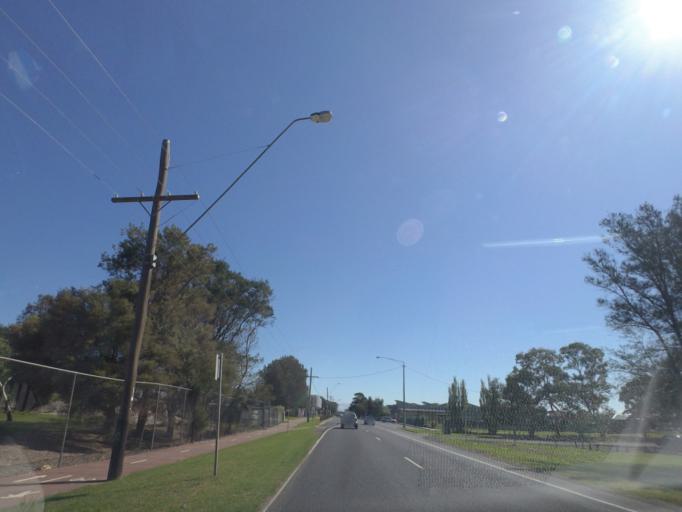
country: AU
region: Victoria
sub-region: Kingston
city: Edithvale
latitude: -38.0345
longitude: 145.1211
